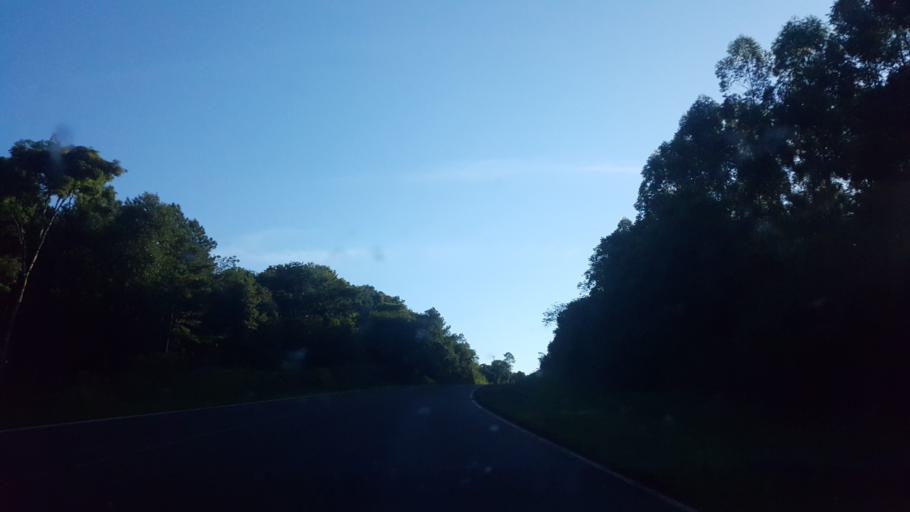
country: AR
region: Misiones
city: Caraguatay
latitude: -26.6640
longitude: -54.7550
